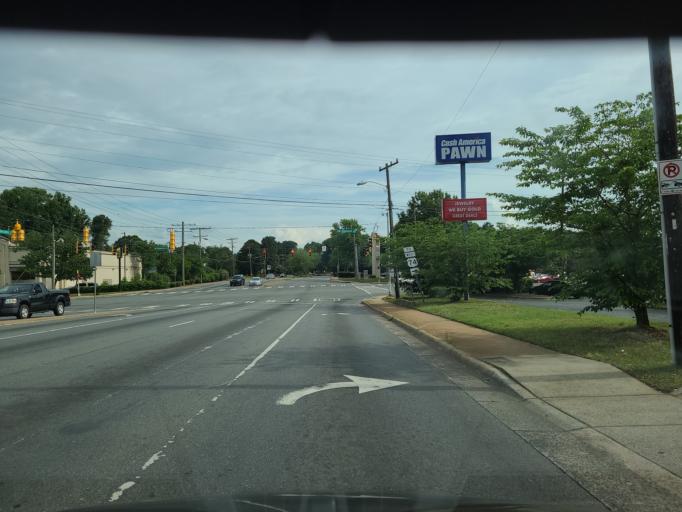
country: US
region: North Carolina
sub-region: Mecklenburg County
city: Charlotte
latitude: 35.2022
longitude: -80.7606
